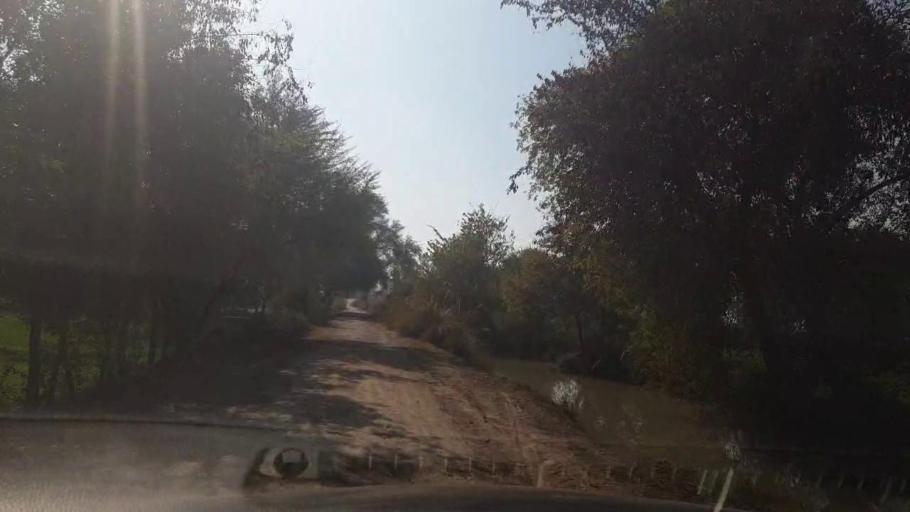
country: PK
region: Sindh
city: Ubauro
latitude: 28.1384
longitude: 69.6839
